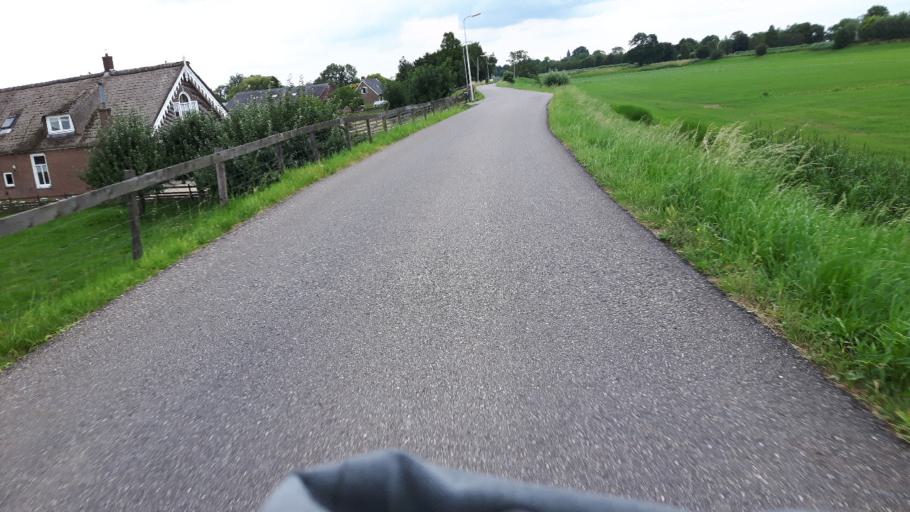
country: NL
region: South Holland
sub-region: Gemeente Vlist
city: Haastrecht
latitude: 52.0060
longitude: 4.7874
